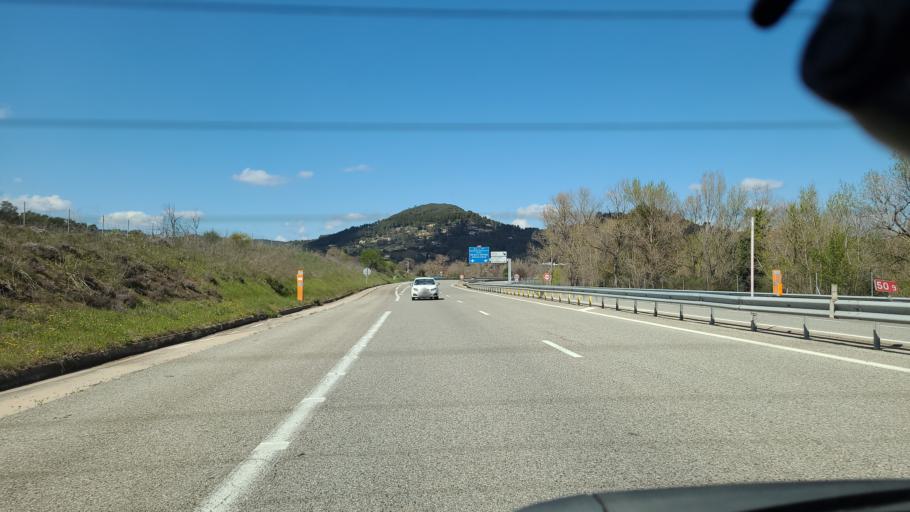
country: FR
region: Provence-Alpes-Cote d'Azur
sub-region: Departement du Var
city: Le Cannet-des-Maures
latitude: 43.3882
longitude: 6.3565
